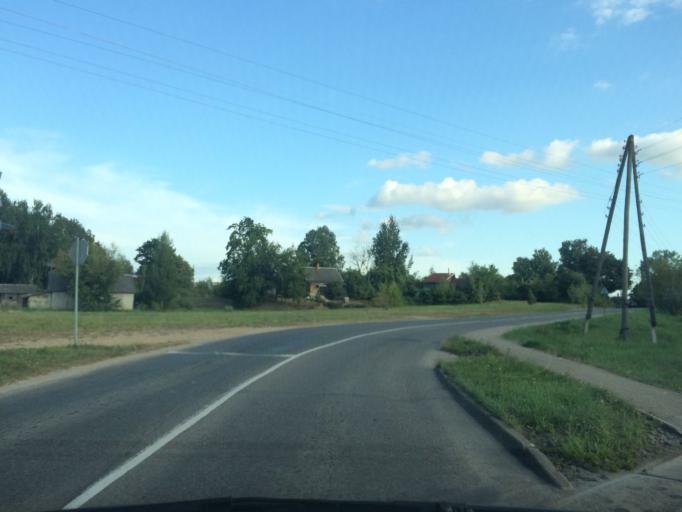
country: LV
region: Rezekne
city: Rezekne
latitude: 56.5168
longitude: 27.3222
